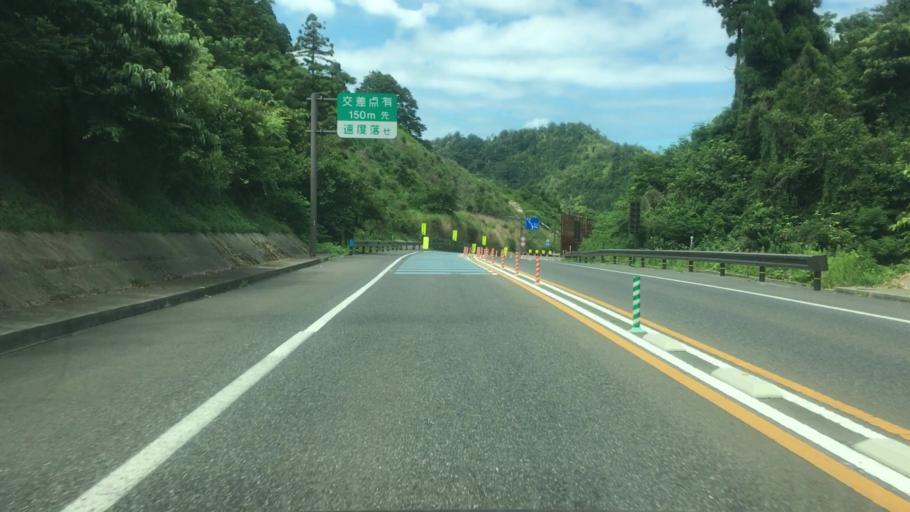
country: JP
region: Tottori
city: Tottori
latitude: 35.5985
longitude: 134.3692
